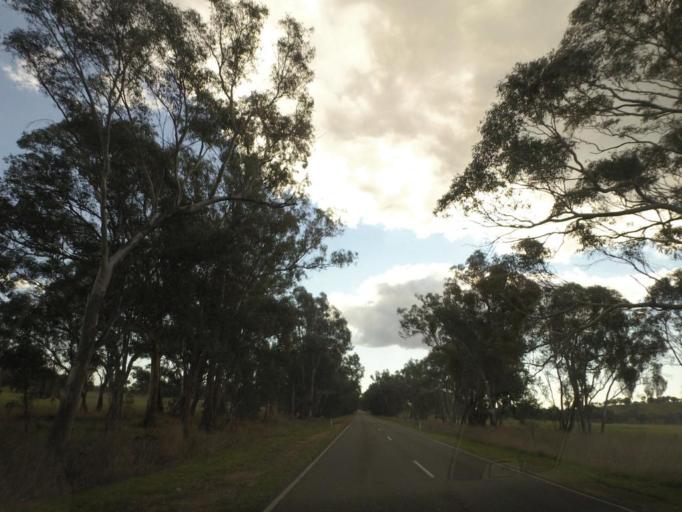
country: AU
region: New South Wales
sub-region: Corowa Shire
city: Howlong
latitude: -36.1906
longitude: 146.6138
